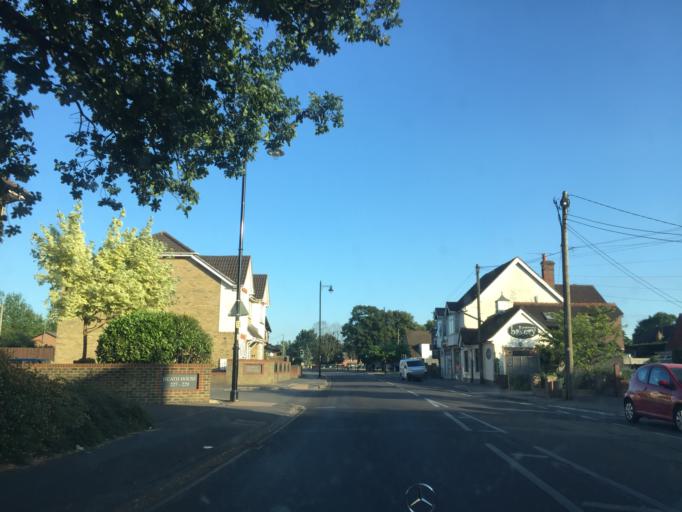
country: GB
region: England
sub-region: Surrey
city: Frimley
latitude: 51.3040
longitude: -0.7288
